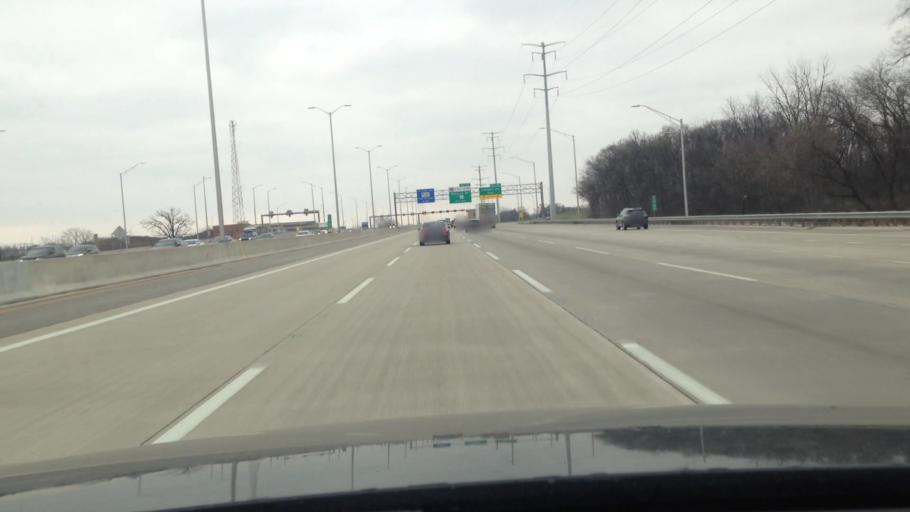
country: US
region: Illinois
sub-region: Cook County
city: Elk Grove Village
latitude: 42.0435
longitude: -87.9903
